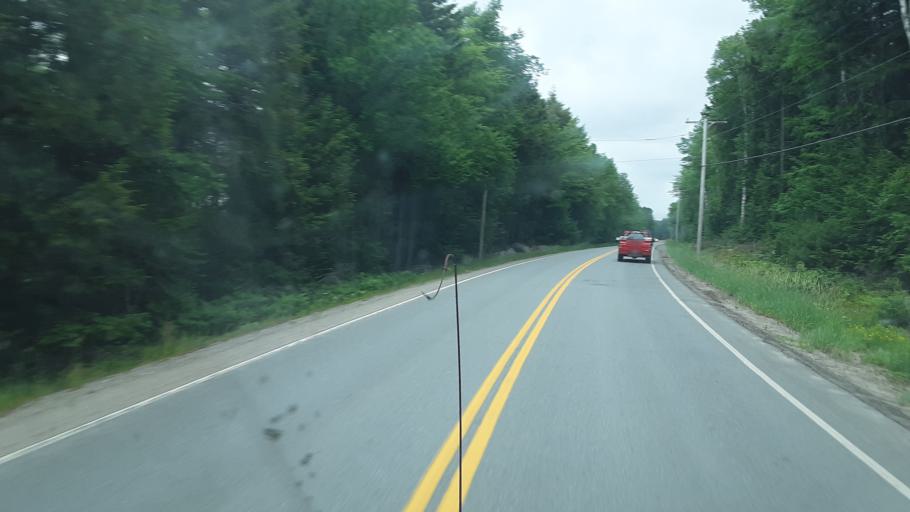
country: US
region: Maine
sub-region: Penobscot County
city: Millinocket
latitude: 45.6804
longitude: -68.7466
